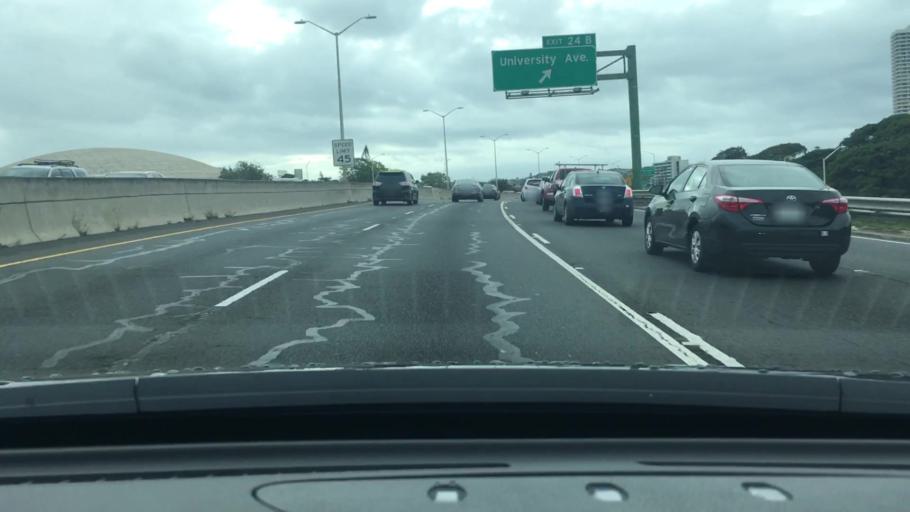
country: US
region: Hawaii
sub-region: Honolulu County
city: Honolulu
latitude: 21.2949
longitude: -157.8219
